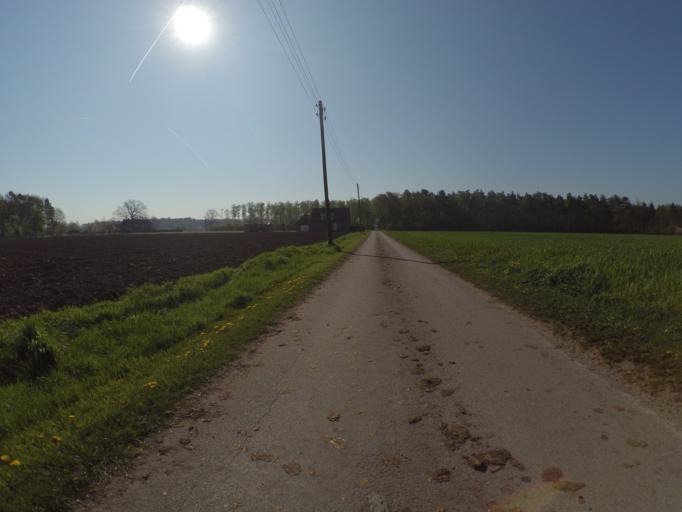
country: DE
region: North Rhine-Westphalia
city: Ludinghausen
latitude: 51.8026
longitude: 7.4273
